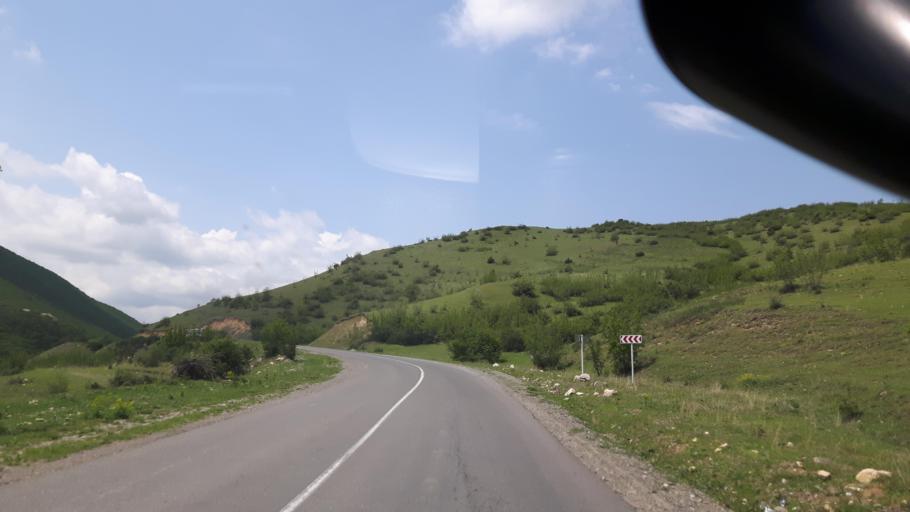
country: GE
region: Mtskheta-Mtianeti
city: Mtskheta
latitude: 41.8378
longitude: 44.5748
